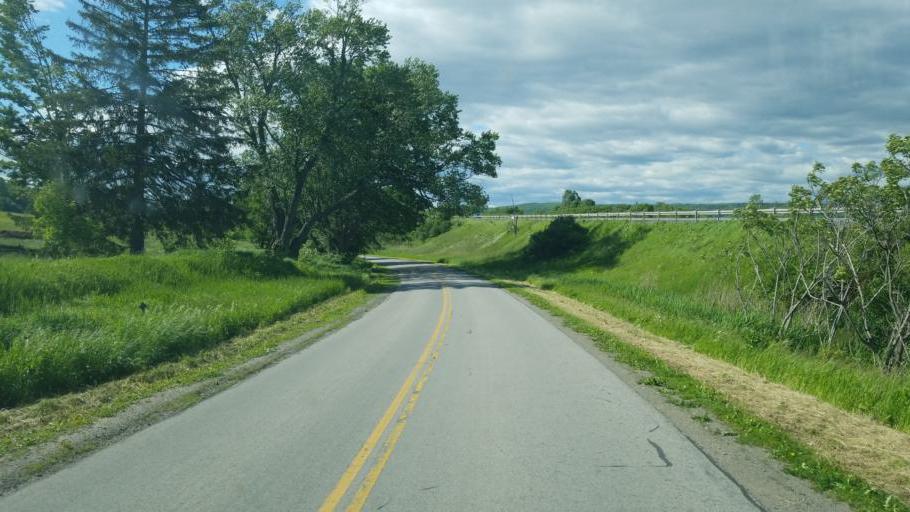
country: US
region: New York
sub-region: Montgomery County
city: Fort Plain
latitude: 42.9561
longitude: -74.6350
